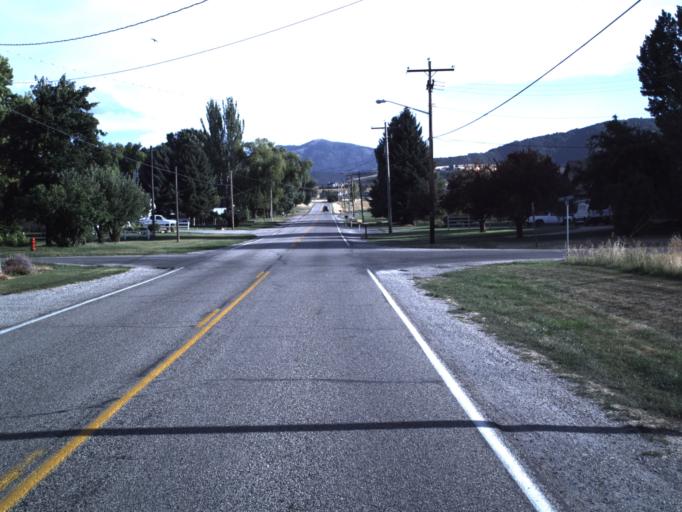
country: US
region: Utah
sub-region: Cache County
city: Wellsville
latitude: 41.6246
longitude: -111.9349
